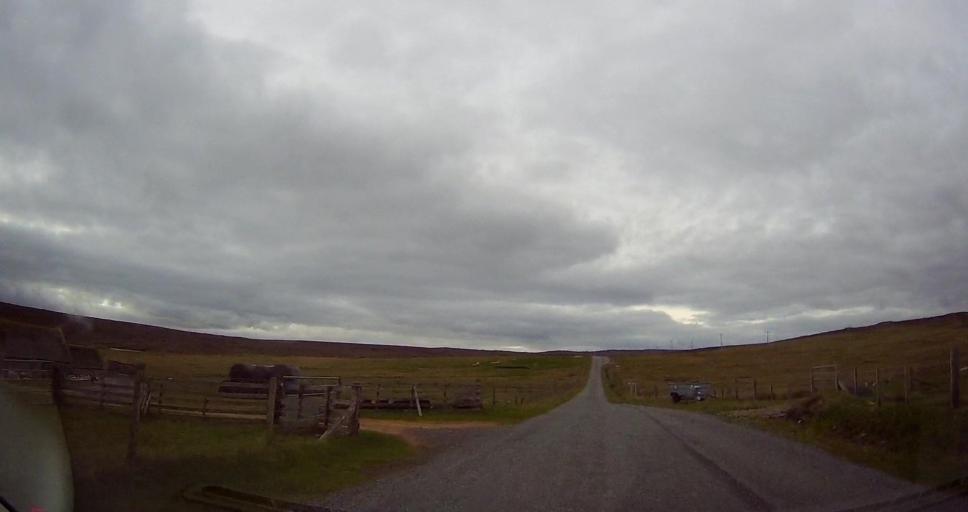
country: GB
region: Scotland
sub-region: Shetland Islands
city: Shetland
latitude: 60.5051
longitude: -1.1044
